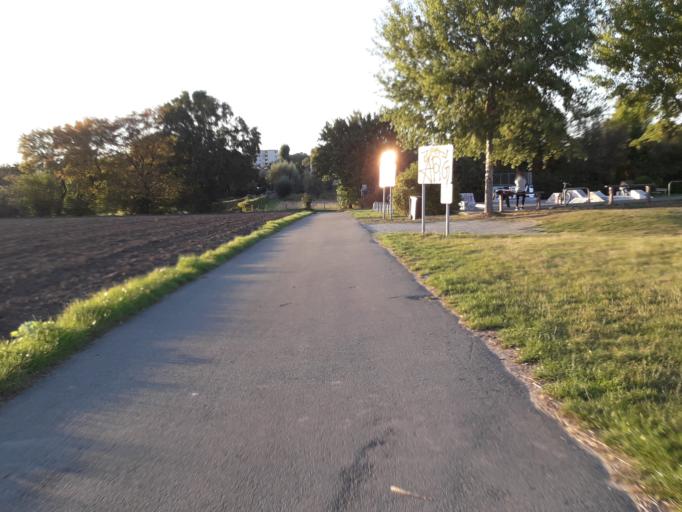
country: DE
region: North Rhine-Westphalia
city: Bad Lippspringe
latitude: 51.7890
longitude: 8.8351
